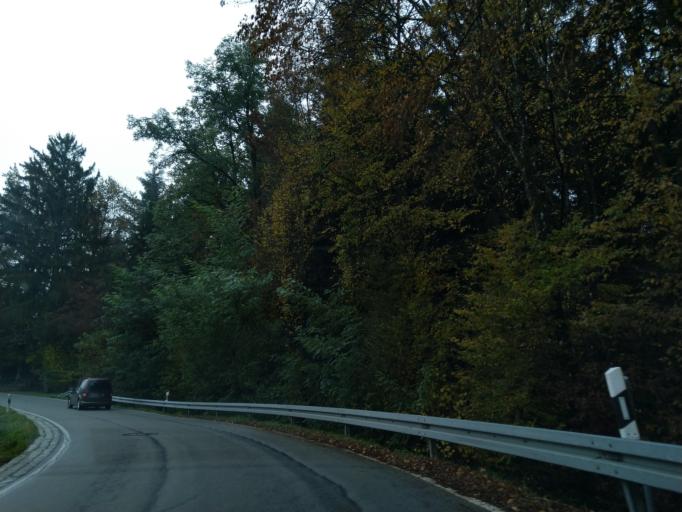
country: DE
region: Bavaria
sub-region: Lower Bavaria
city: Auerbach
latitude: 48.7970
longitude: 13.0983
